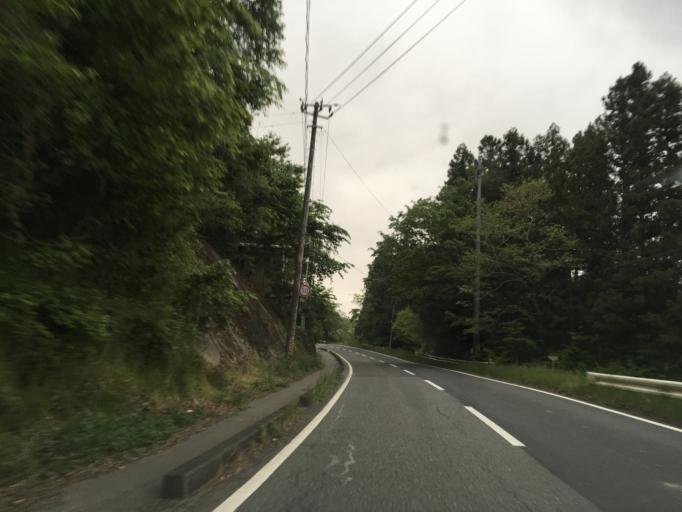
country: JP
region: Miyagi
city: Wakuya
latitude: 38.7305
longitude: 141.2990
